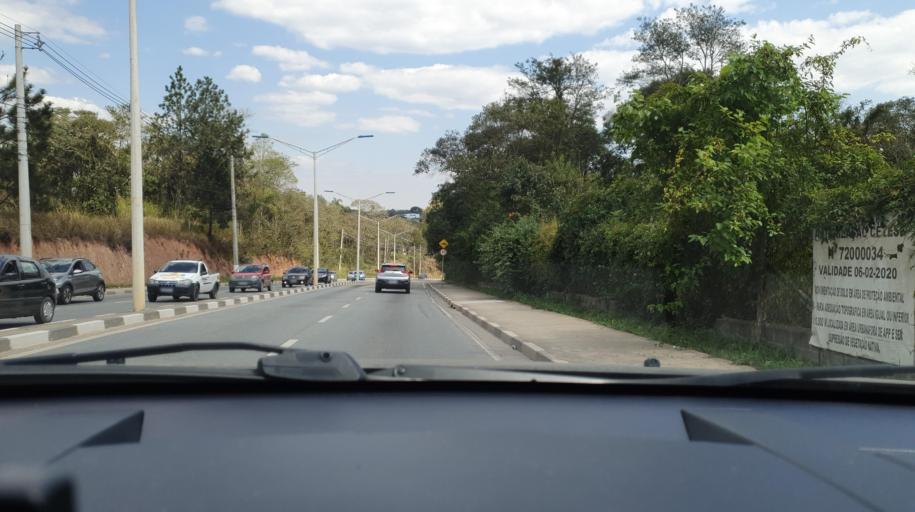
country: BR
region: Sao Paulo
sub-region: Vargem Grande Paulista
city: Vargem Grande Paulista
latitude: -23.6593
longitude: -47.0026
